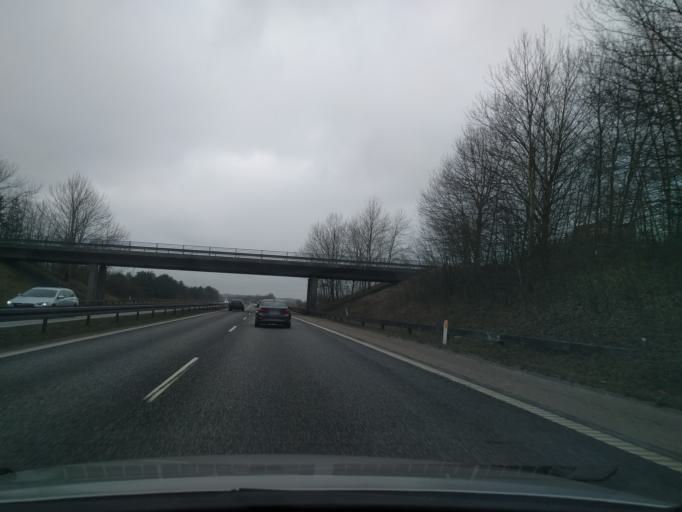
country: DK
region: Zealand
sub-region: Soro Kommune
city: Soro
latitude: 55.4534
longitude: 11.5480
